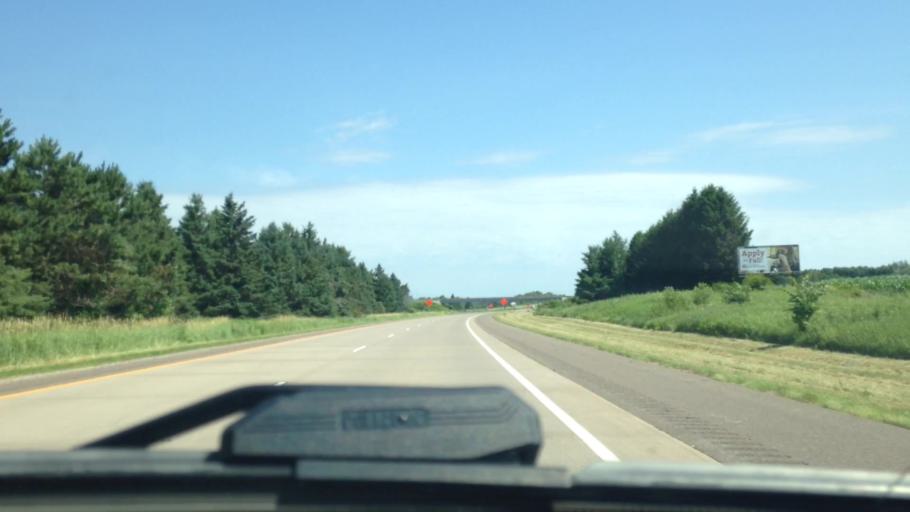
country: US
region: Wisconsin
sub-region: Barron County
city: Rice Lake
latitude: 45.5619
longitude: -91.7655
